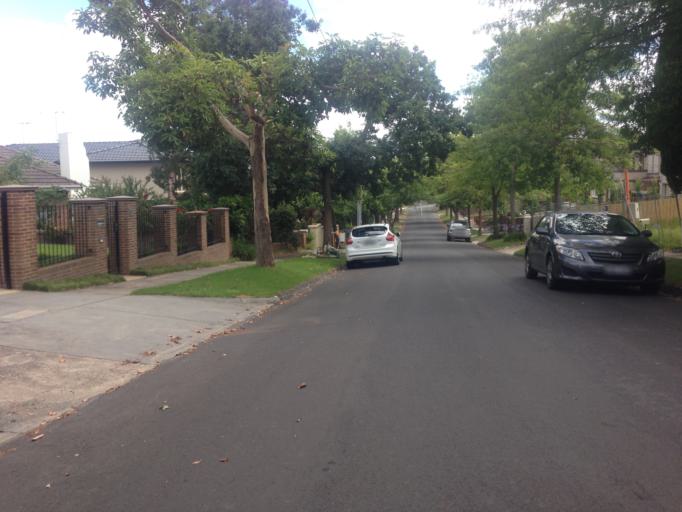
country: AU
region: Victoria
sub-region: Boroondara
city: Balwyn North
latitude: -37.7922
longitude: 145.0782
